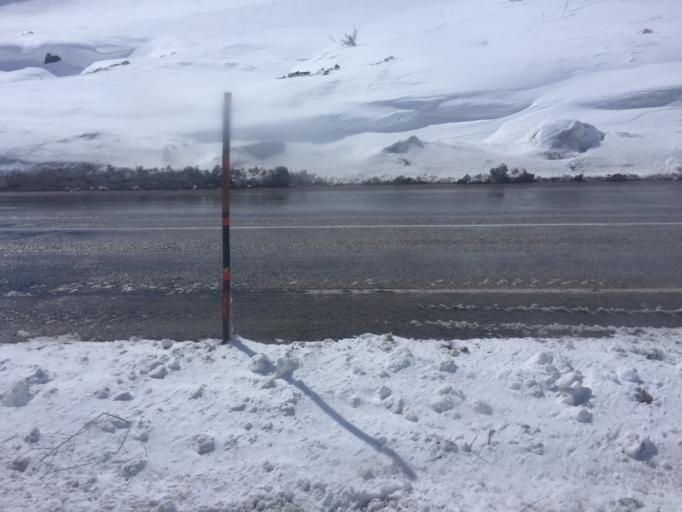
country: TR
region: Kahramanmaras
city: Goksun
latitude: 38.1995
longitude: 36.4536
